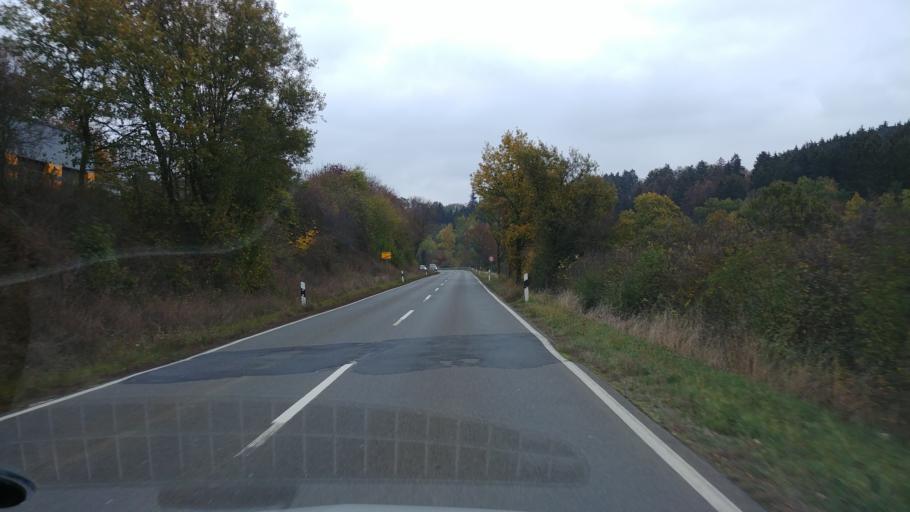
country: DE
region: Hesse
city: Taunusstein
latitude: 50.1490
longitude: 8.1574
